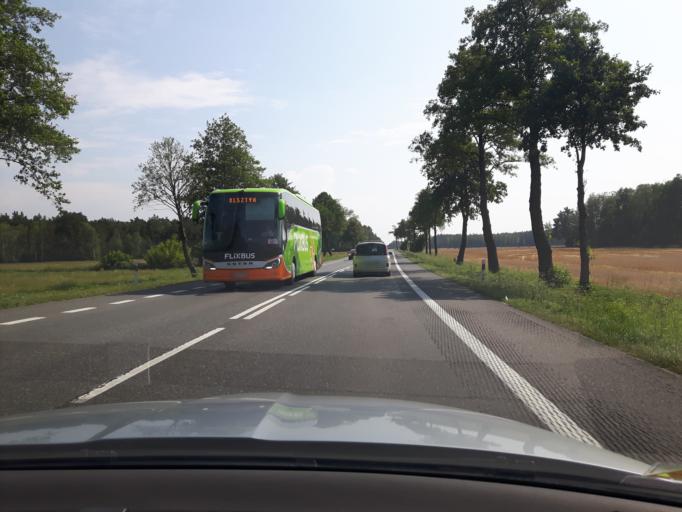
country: PL
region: Masovian Voivodeship
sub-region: Powiat mlawski
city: Strzegowo
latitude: 52.9293
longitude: 20.2858
